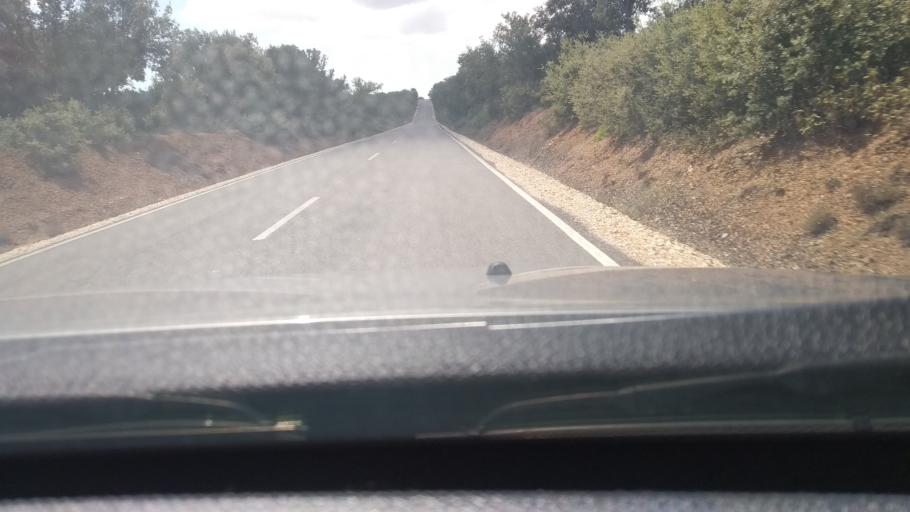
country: ES
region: Castille and Leon
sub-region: Provincia de Burgos
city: Avellanosa de Muno
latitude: 41.9674
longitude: -3.8138
